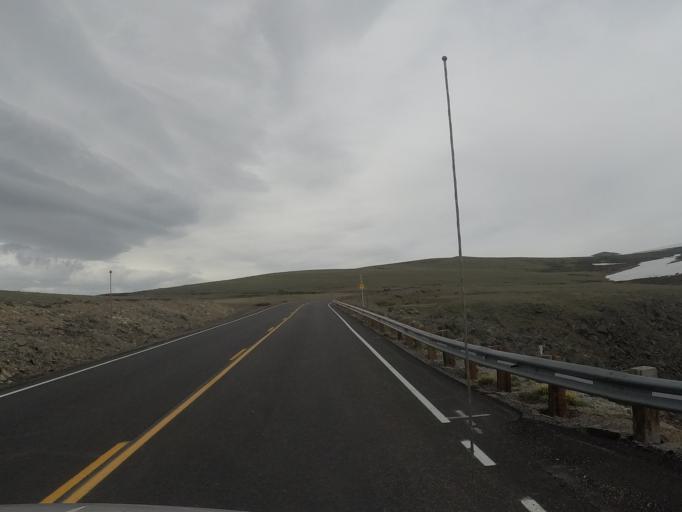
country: US
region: Montana
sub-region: Carbon County
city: Red Lodge
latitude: 45.0270
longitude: -109.4071
